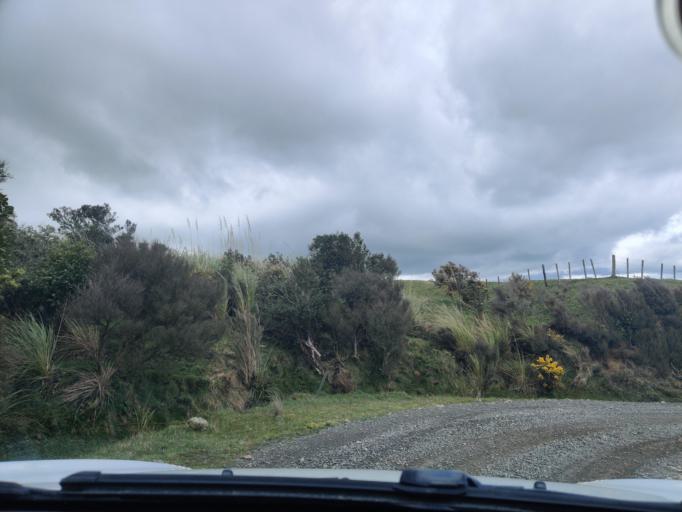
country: NZ
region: Manawatu-Wanganui
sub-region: Palmerston North City
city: Palmerston North
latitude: -40.2756
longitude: 175.8529
